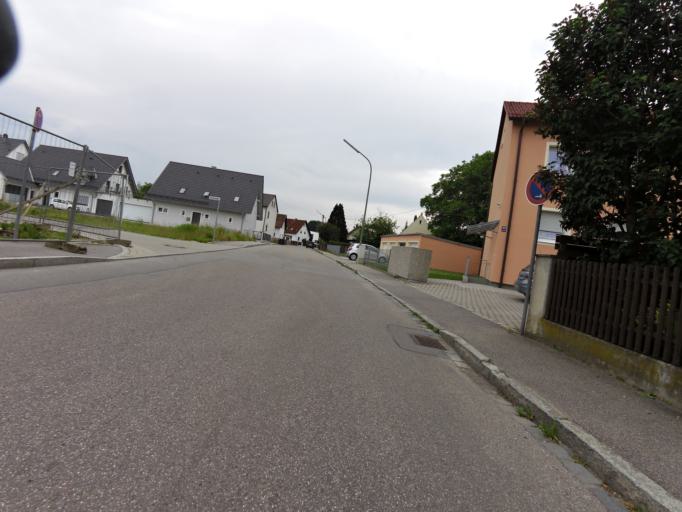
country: DE
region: Bavaria
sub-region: Upper Bavaria
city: Moosburg
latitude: 48.4629
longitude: 11.9402
